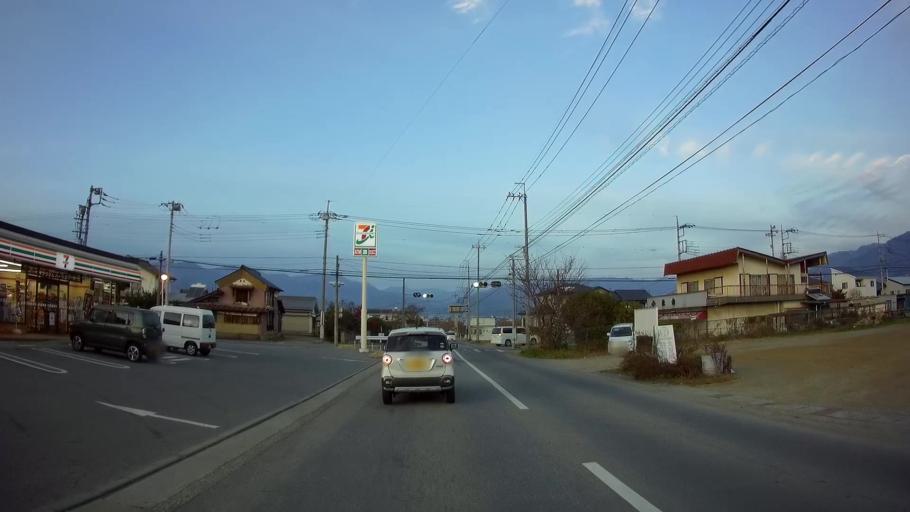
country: JP
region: Yamanashi
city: Isawa
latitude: 35.6568
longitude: 138.6914
